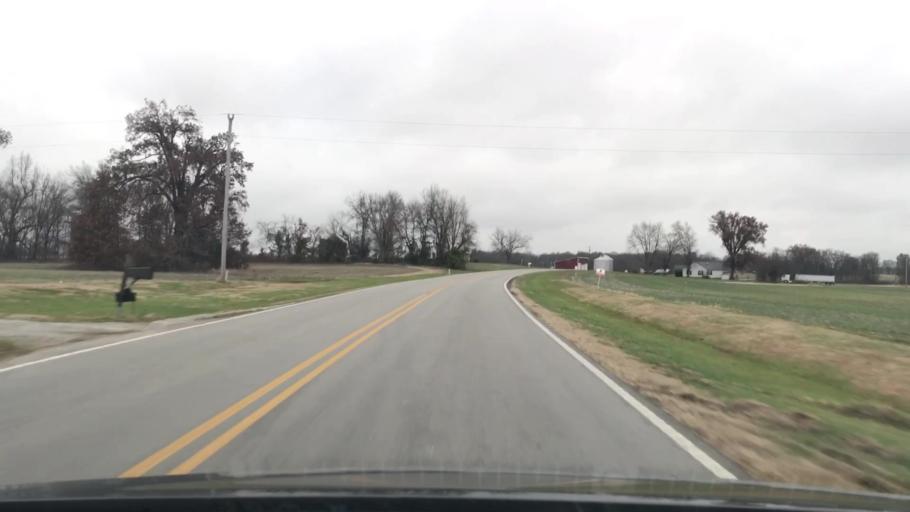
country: US
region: Kentucky
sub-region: Todd County
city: Guthrie
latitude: 36.7303
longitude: -87.1897
